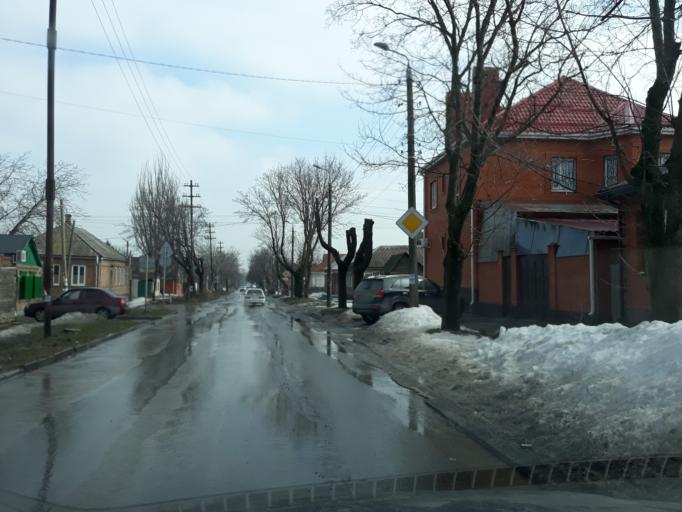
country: RU
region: Rostov
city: Taganrog
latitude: 47.2166
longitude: 38.8956
